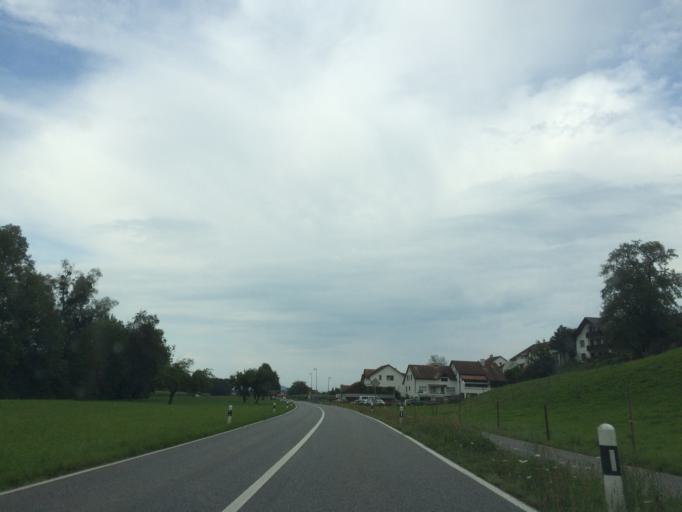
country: LI
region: Gamprin
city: Gamprin
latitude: 47.2245
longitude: 9.5095
